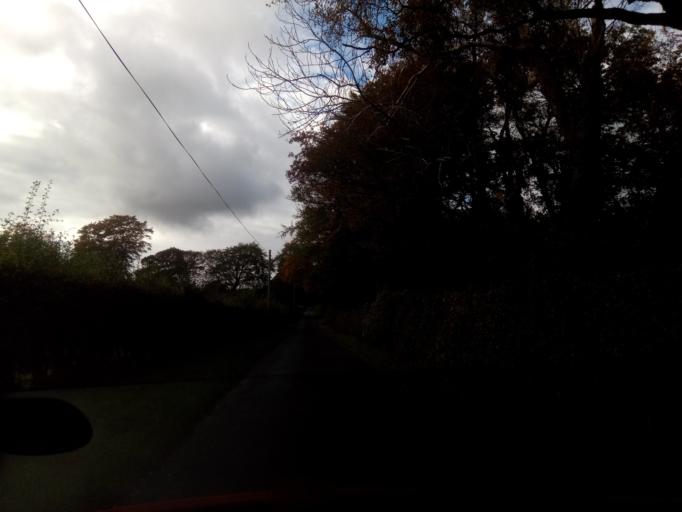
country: GB
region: Scotland
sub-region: The Scottish Borders
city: Galashiels
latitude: 55.6720
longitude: -2.8211
